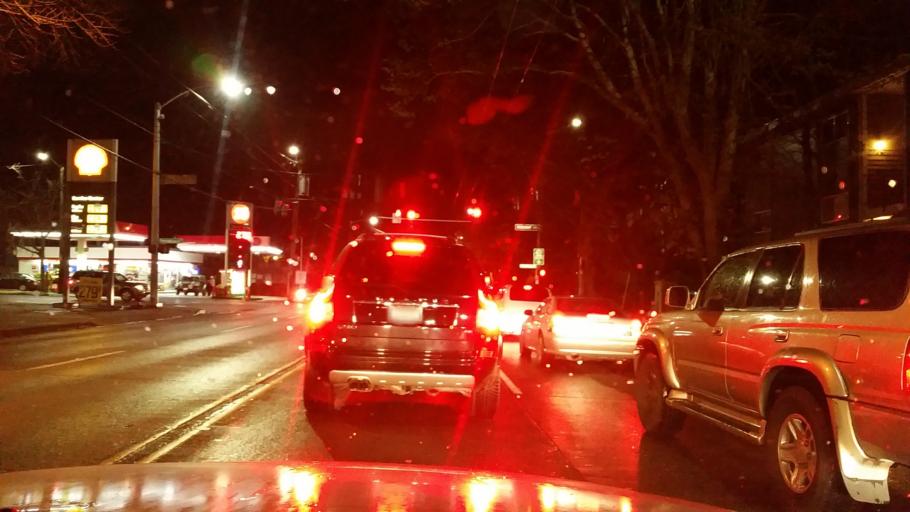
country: US
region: Washington
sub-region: King County
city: Seattle
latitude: 47.6621
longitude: -122.3507
